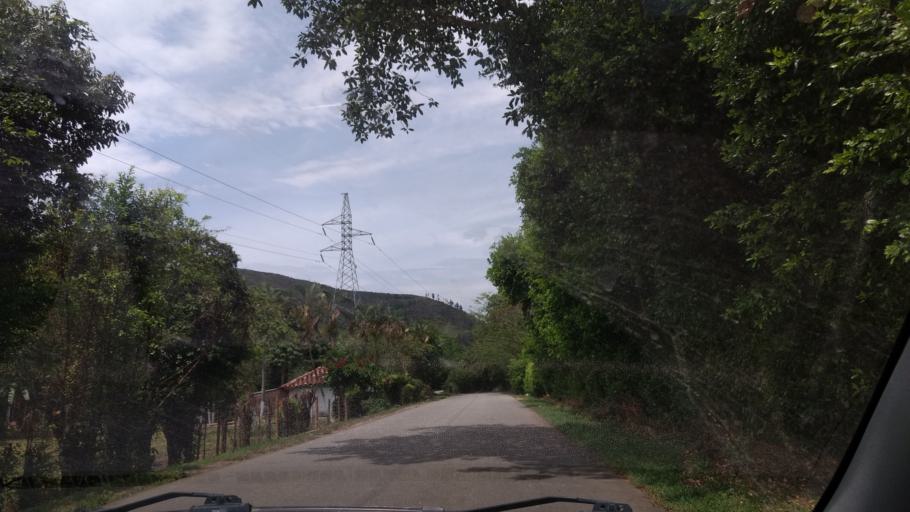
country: CO
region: Cauca
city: Buenos Aires
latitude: 3.0720
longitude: -76.6538
